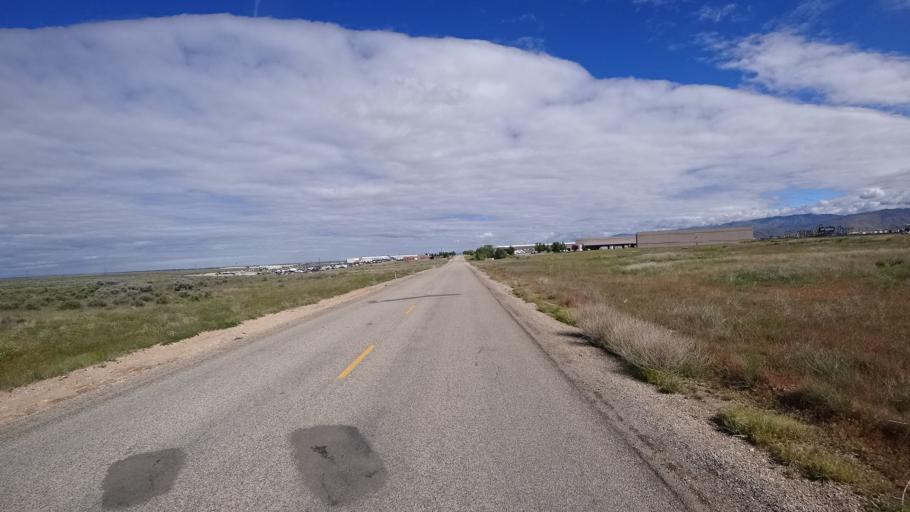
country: US
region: Idaho
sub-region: Ada County
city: Boise
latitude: 43.5295
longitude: -116.1568
